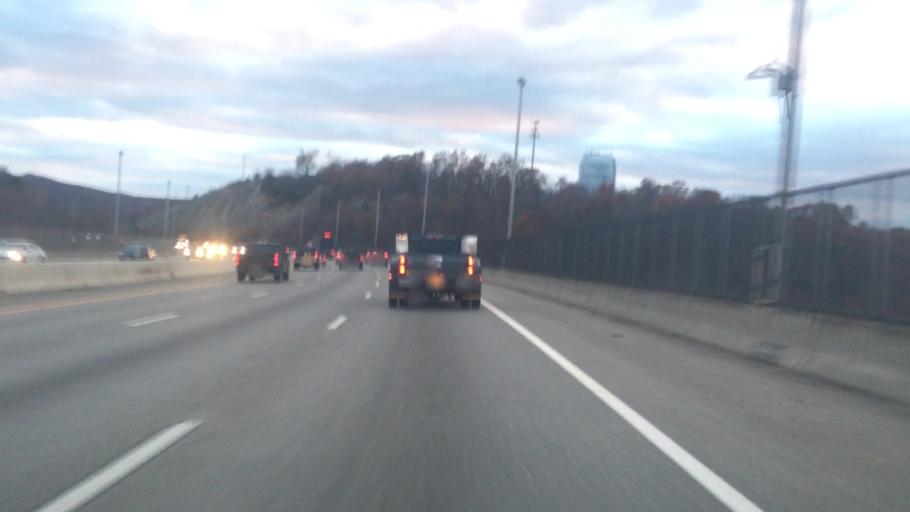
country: US
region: New Jersey
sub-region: Passaic County
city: Wanaque
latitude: 41.0268
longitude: -74.2862
